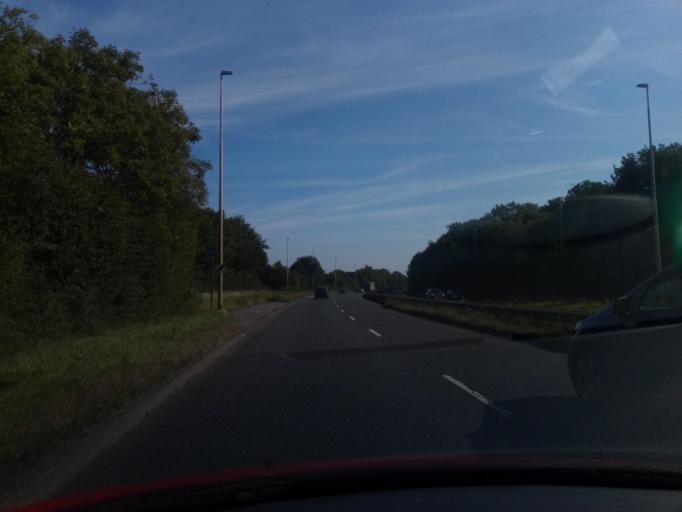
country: GB
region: England
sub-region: South Tyneside
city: The Boldons
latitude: 54.9076
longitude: -1.4703
